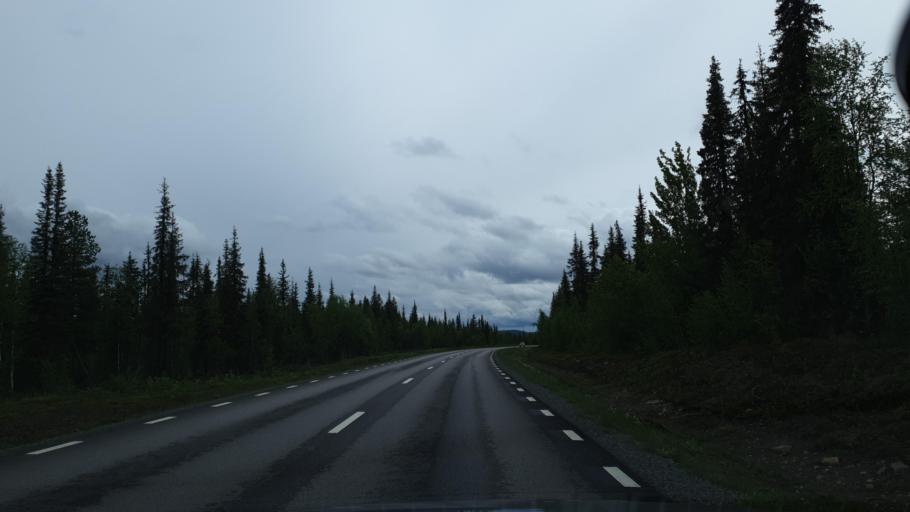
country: SE
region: Norrbotten
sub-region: Gallivare Kommun
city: Malmberget
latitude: 67.5605
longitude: 21.1488
